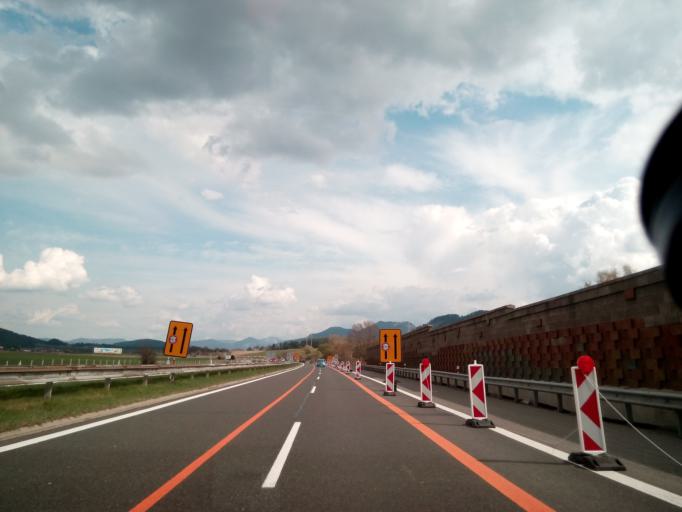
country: SK
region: Zilinsky
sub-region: Okres Liptovsky Mikulas
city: Liptovsky Mikulas
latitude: 49.0618
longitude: 19.6535
